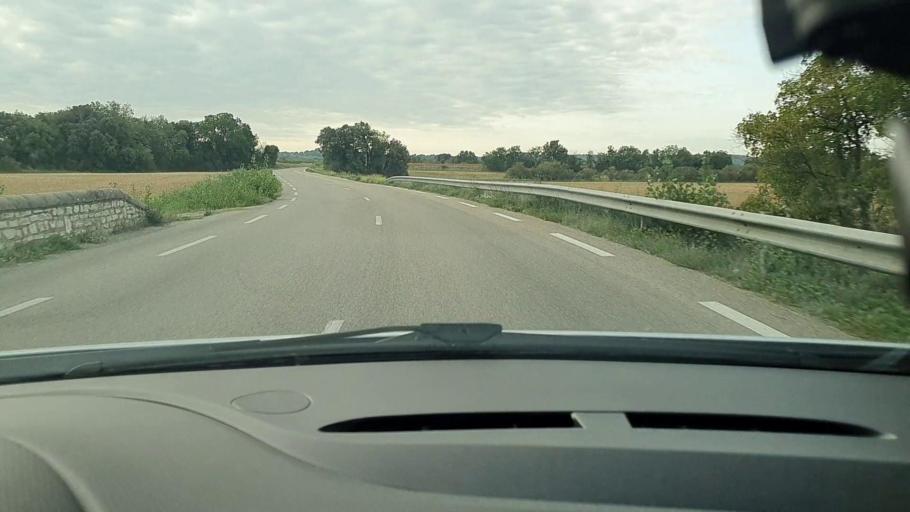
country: FR
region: Languedoc-Roussillon
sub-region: Departement du Gard
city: Mons
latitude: 44.0829
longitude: 4.2181
